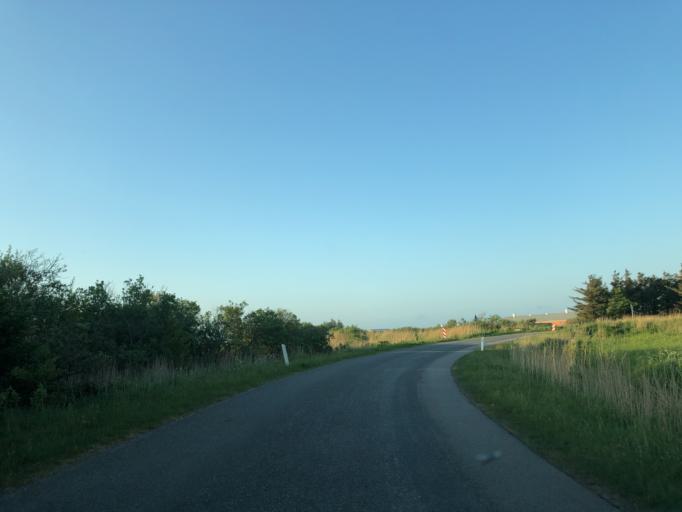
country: DK
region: Central Jutland
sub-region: Ringkobing-Skjern Kommune
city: Ringkobing
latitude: 56.2031
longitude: 8.1598
